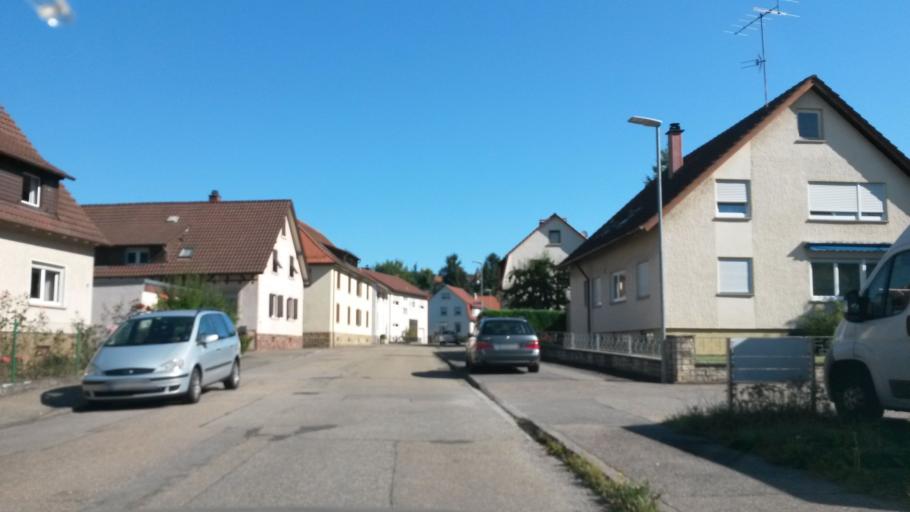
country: DE
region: Baden-Wuerttemberg
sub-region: Karlsruhe Region
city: Eisingen
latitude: 48.9596
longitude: 8.6407
